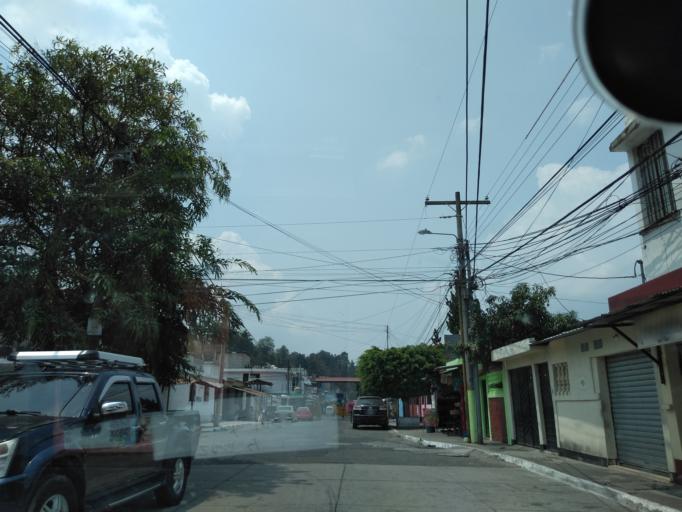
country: GT
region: Guatemala
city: Petapa
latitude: 14.5232
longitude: -90.5407
